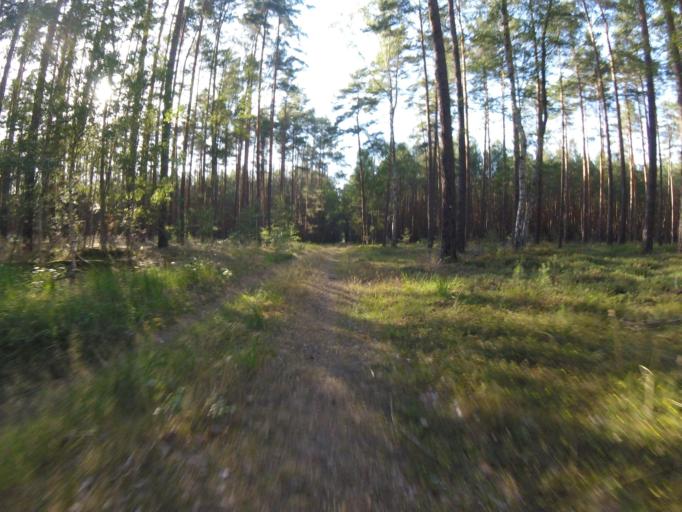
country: DE
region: Berlin
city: Schmockwitz
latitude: 52.3366
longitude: 13.7012
